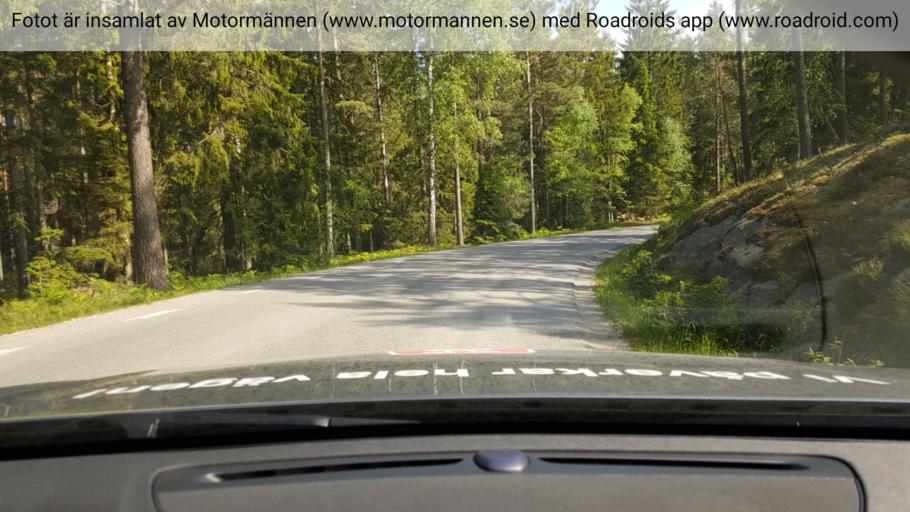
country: SE
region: Stockholm
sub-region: Varmdo Kommun
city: Mortnas
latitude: 59.2527
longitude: 18.4536
